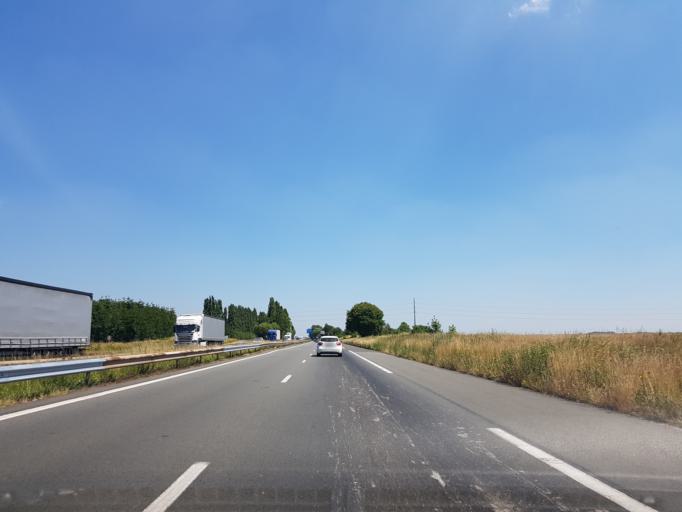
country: FR
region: Nord-Pas-de-Calais
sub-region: Departement du Nord
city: Lieu-Saint-Amand
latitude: 50.2849
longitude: 3.3510
